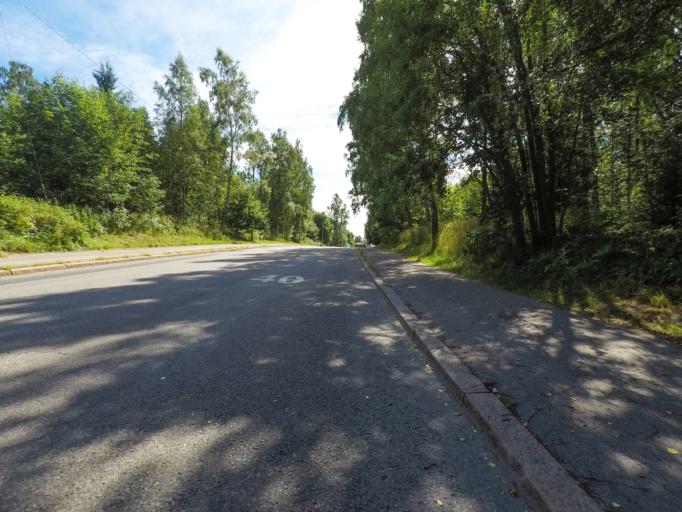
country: FI
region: Uusimaa
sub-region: Helsinki
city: Vantaa
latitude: 60.2053
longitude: 25.0582
